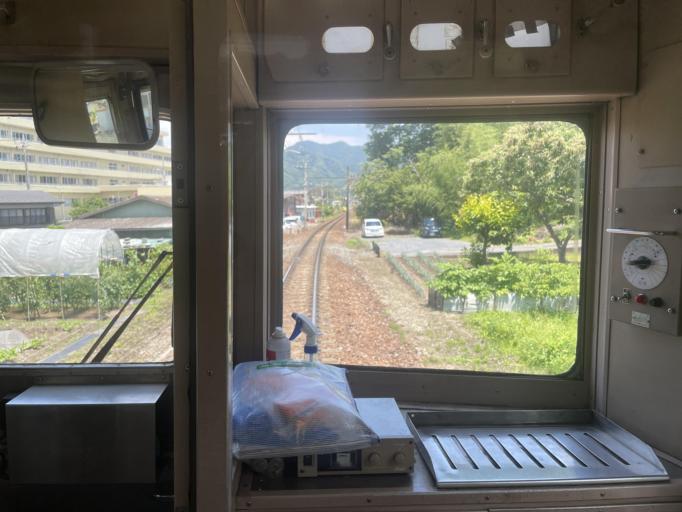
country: JP
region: Saitama
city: Chichibu
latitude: 36.0763
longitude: 139.1002
